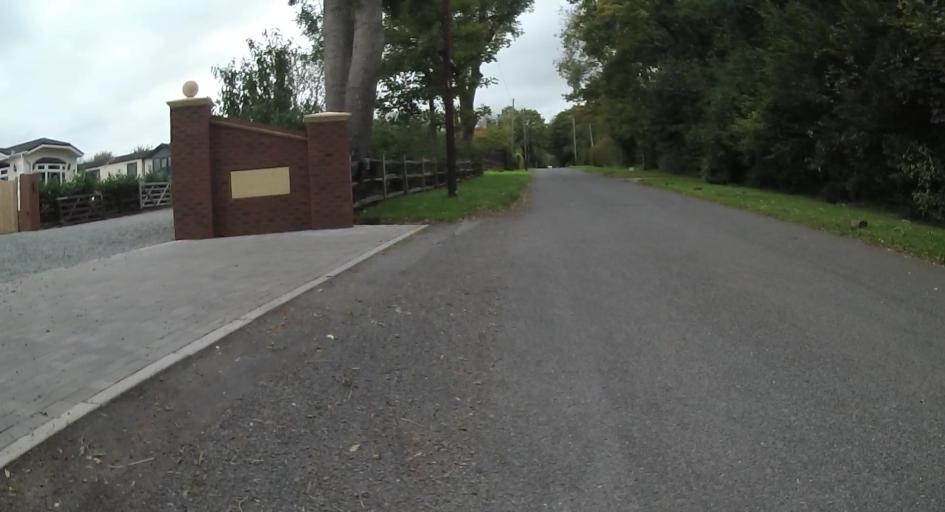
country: GB
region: England
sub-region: Hampshire
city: Four Marks
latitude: 51.1029
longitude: -1.0303
